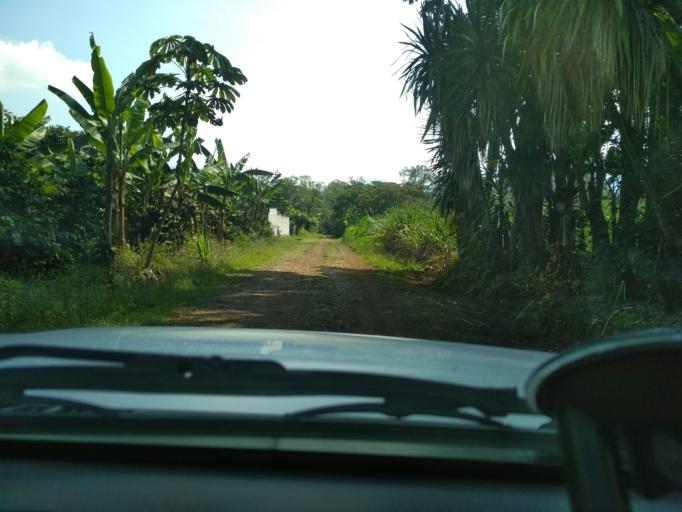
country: MX
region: Veracruz
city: Monte Blanco
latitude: 18.9790
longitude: -97.0114
